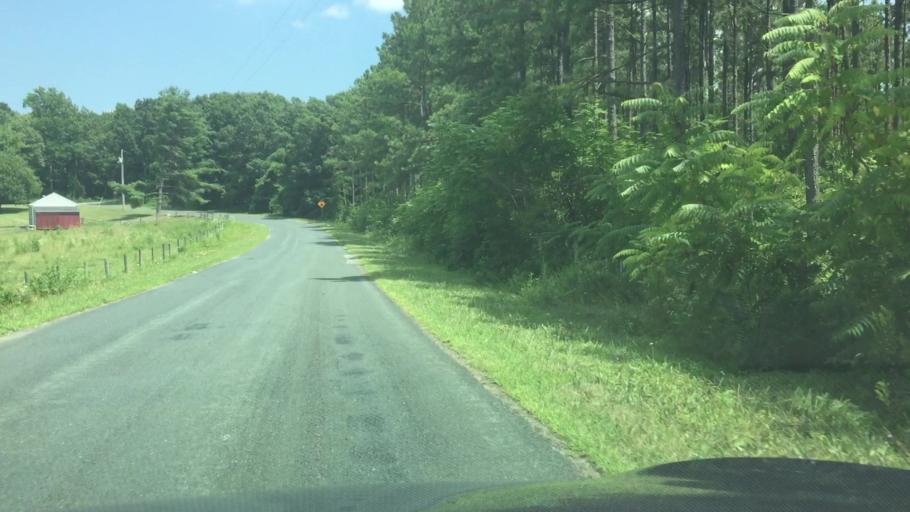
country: US
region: Virginia
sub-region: Appomattox County
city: Appomattox
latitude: 37.3208
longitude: -78.8524
